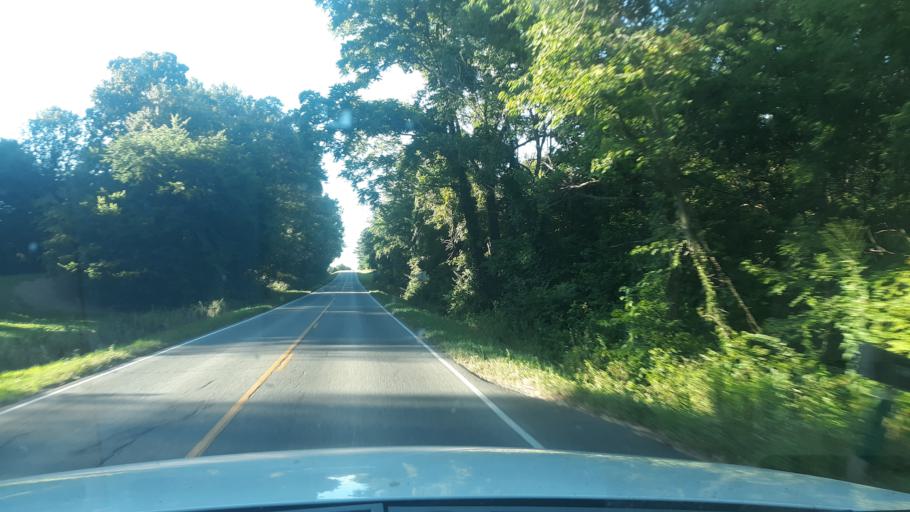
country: US
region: Illinois
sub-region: Saline County
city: Harrisburg
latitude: 37.8478
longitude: -88.6054
